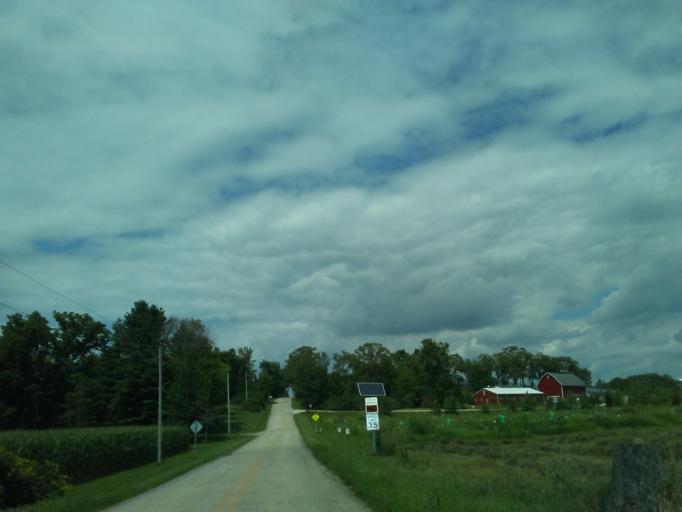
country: US
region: Wisconsin
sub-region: Dane County
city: Verona
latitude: 42.9991
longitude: -89.5781
